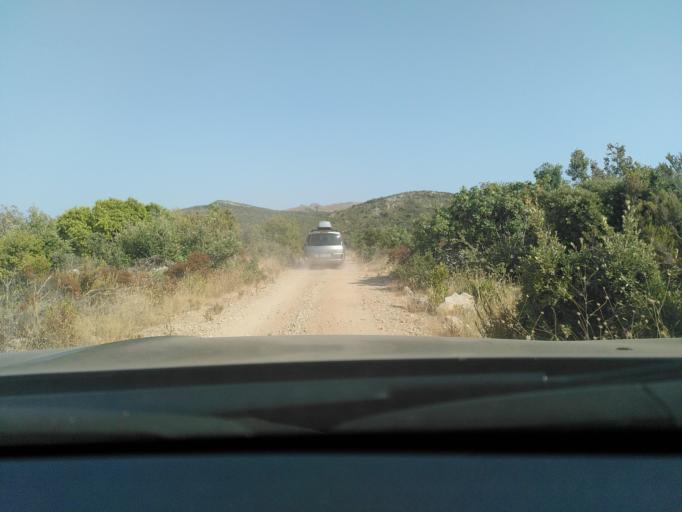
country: HR
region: Splitsko-Dalmatinska
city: Stari Grad
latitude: 43.1626
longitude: 16.5522
